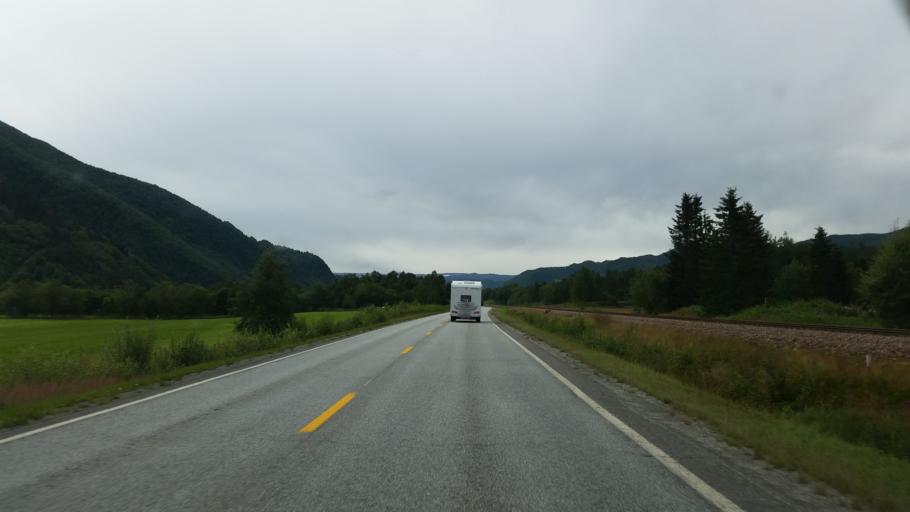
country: NO
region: Nordland
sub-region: Saltdal
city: Rognan
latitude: 67.0411
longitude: 15.3783
